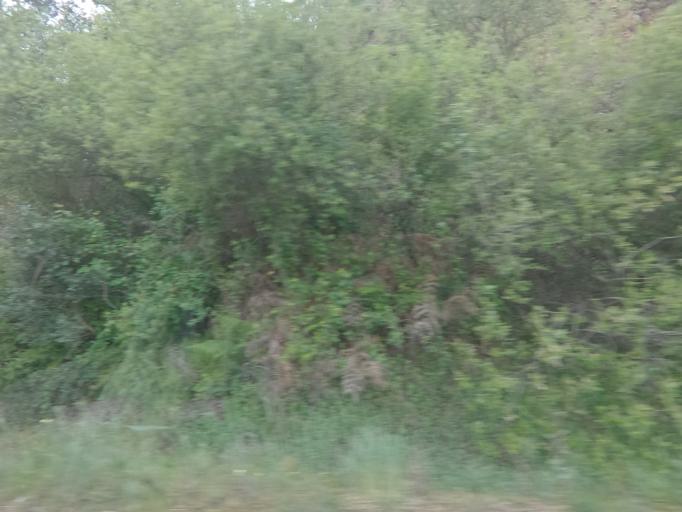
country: ES
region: Extremadura
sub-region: Provincia de Badajoz
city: Puebla de Obando
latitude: 39.1859
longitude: -6.6005
